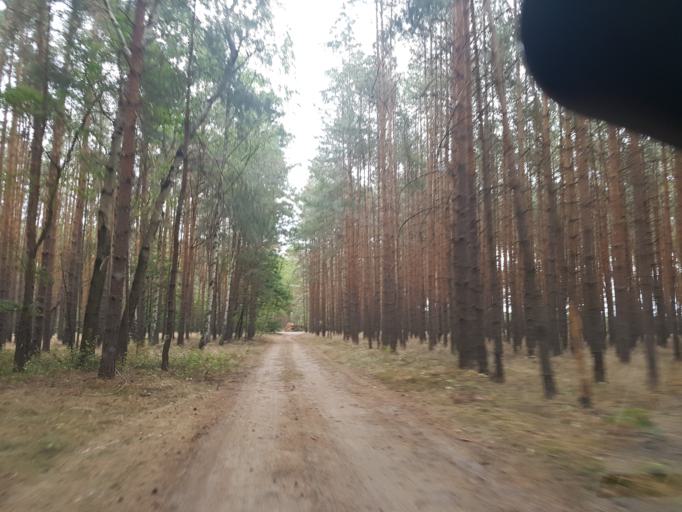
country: DE
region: Brandenburg
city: Schilda
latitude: 51.5680
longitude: 13.3316
